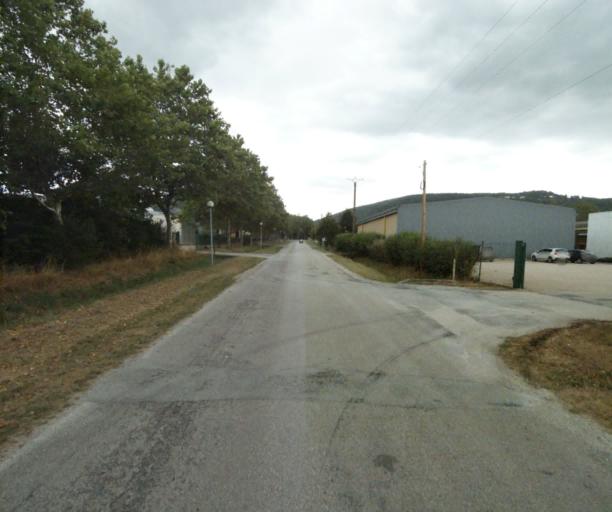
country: FR
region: Midi-Pyrenees
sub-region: Departement du Tarn
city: Soreze
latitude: 43.4538
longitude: 2.0492
